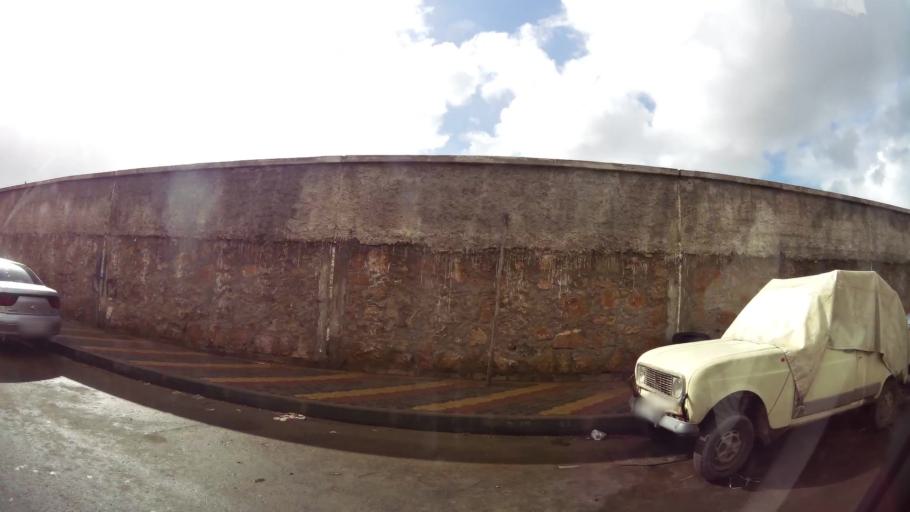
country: MA
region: Grand Casablanca
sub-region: Casablanca
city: Casablanca
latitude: 33.5598
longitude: -7.6797
